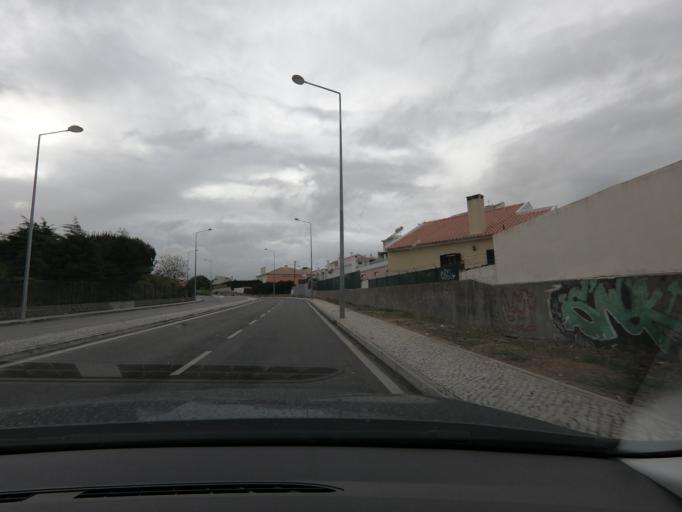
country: PT
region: Lisbon
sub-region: Cascais
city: Sao Domingos de Rana
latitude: 38.7108
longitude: -9.3341
